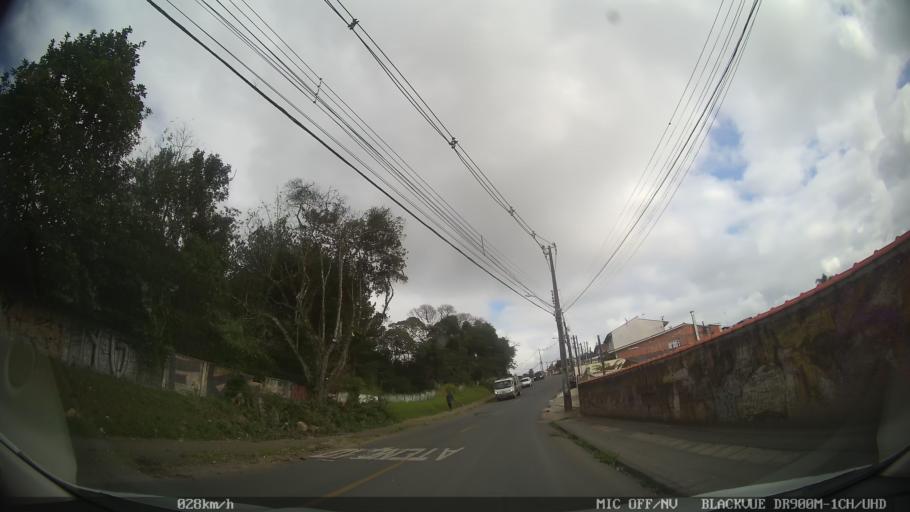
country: BR
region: Parana
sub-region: Almirante Tamandare
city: Almirante Tamandare
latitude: -25.3533
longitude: -49.2564
